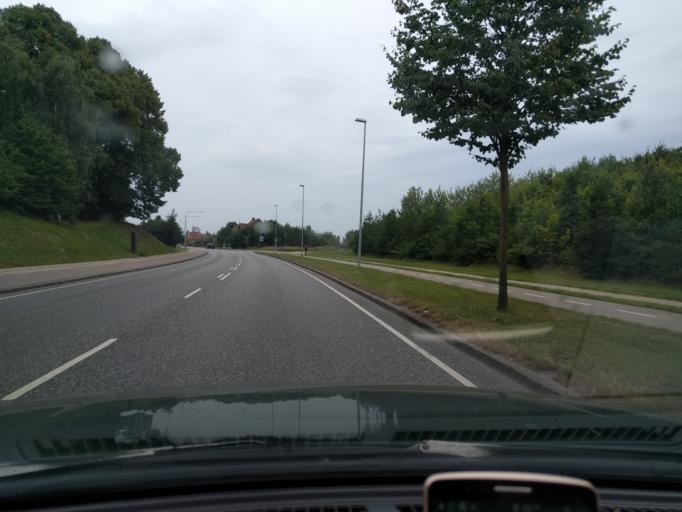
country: DK
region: Zealand
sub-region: Slagelse Kommune
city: Korsor
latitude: 55.3459
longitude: 11.1405
